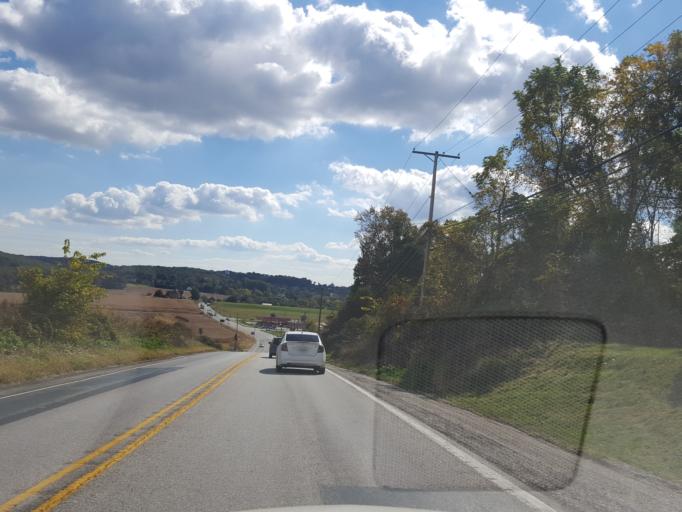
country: US
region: Pennsylvania
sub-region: York County
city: Stonybrook
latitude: 39.9507
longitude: -76.6487
